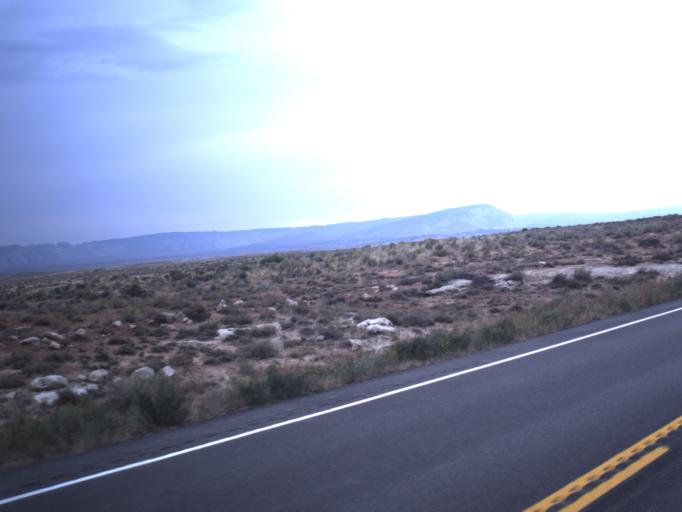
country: US
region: Utah
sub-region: Uintah County
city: Naples
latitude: 40.2622
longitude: -109.4437
